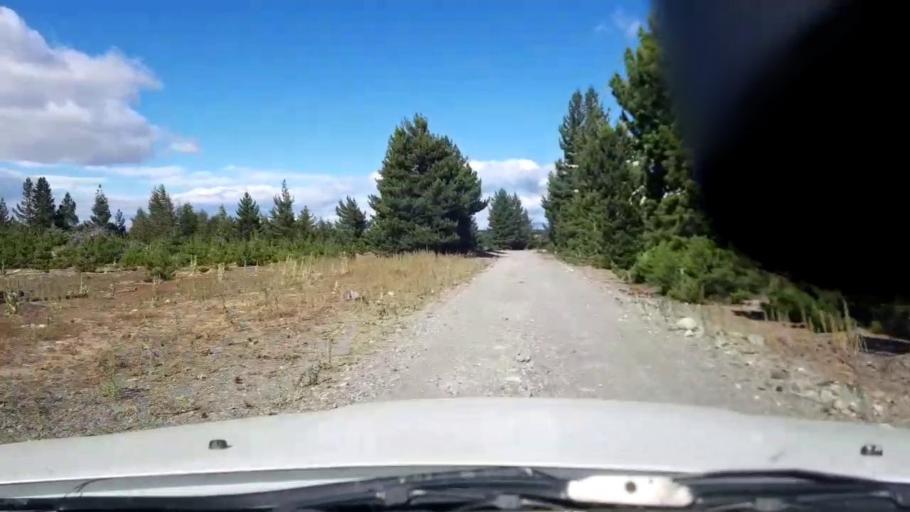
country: NZ
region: Canterbury
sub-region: Timaru District
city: Pleasant Point
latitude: -44.0144
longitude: 170.4726
